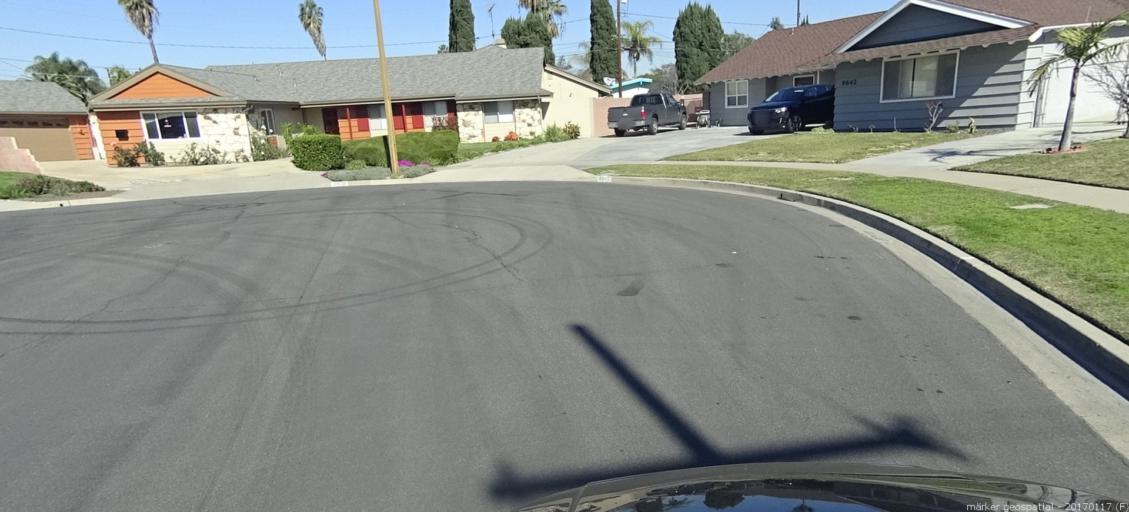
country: US
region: California
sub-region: Orange County
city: Stanton
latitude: 33.8228
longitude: -117.9628
